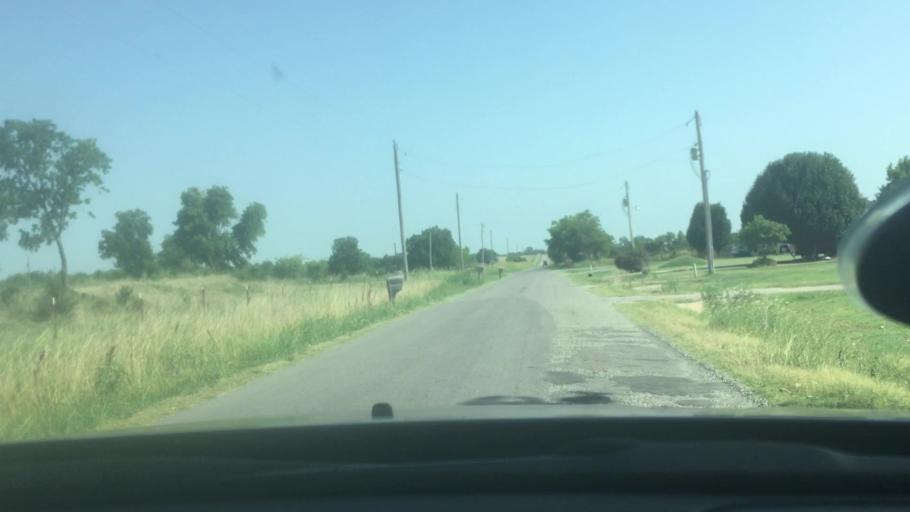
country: US
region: Oklahoma
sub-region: Bryan County
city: Calera
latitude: 33.9678
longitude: -96.4656
